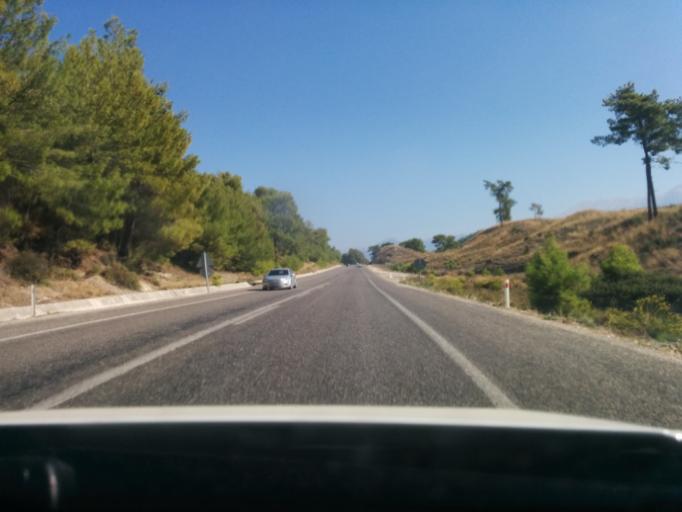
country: TR
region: Mugla
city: Esen
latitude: 36.4784
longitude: 29.3064
